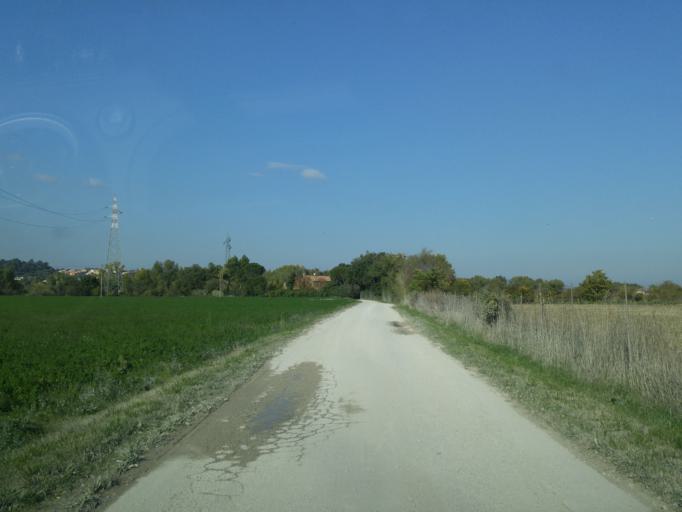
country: IT
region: The Marches
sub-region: Provincia di Pesaro e Urbino
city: Villanova
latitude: 43.7403
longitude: 12.9219
